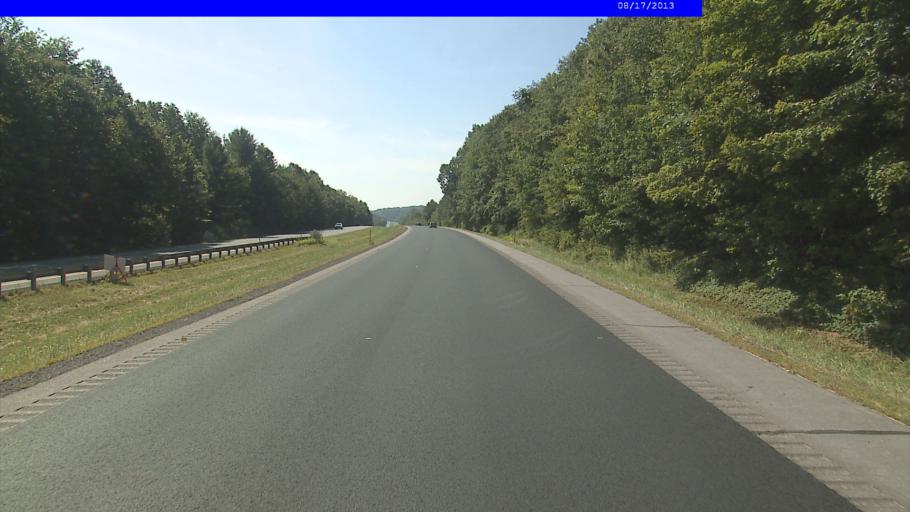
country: US
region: Vermont
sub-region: Windham County
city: Bellows Falls
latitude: 43.0668
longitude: -72.4703
